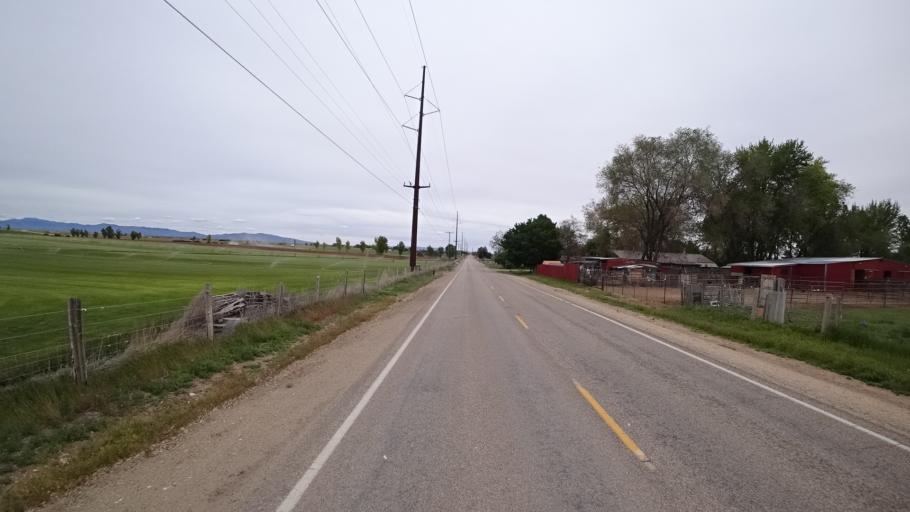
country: US
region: Idaho
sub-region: Ada County
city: Kuna
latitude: 43.4886
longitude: -116.3191
